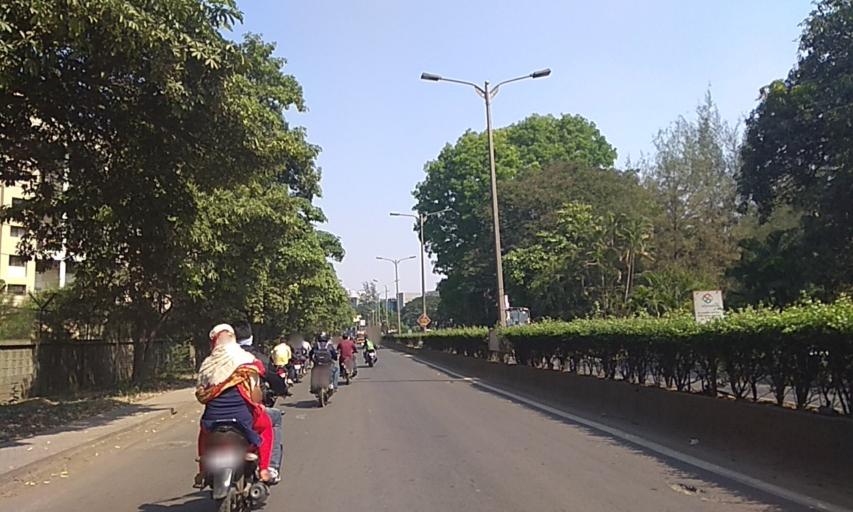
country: IN
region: Maharashtra
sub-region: Pune Division
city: Pune
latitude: 18.5097
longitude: 73.9308
